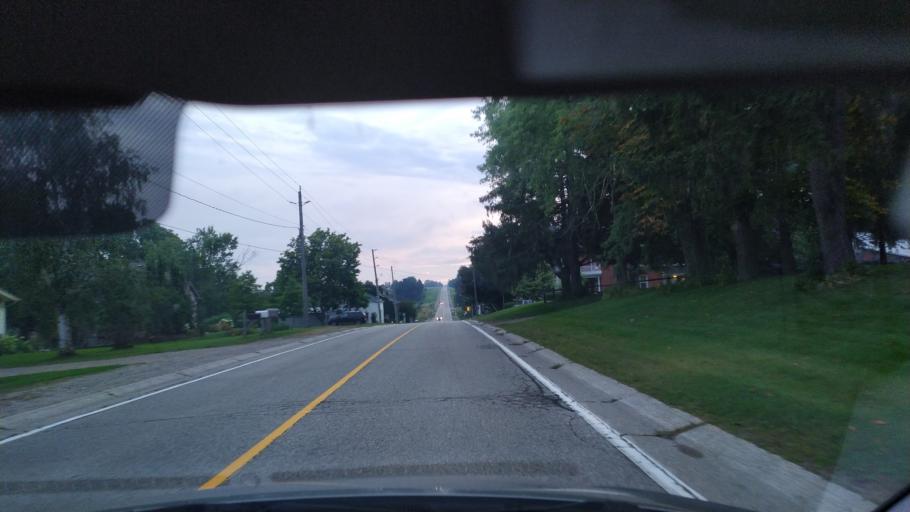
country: CA
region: Ontario
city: Kitchener
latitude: 43.3101
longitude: -80.5783
